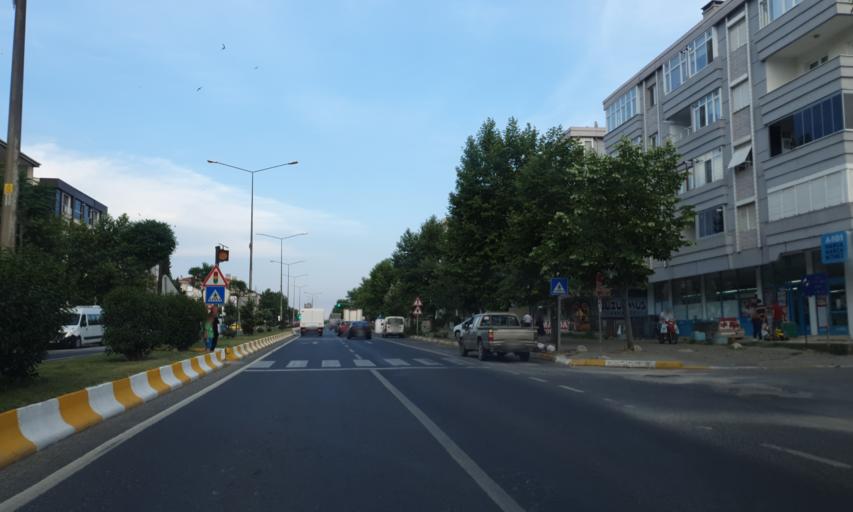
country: TR
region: Kirklareli
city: Luleburgaz
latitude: 41.4019
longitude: 27.3689
